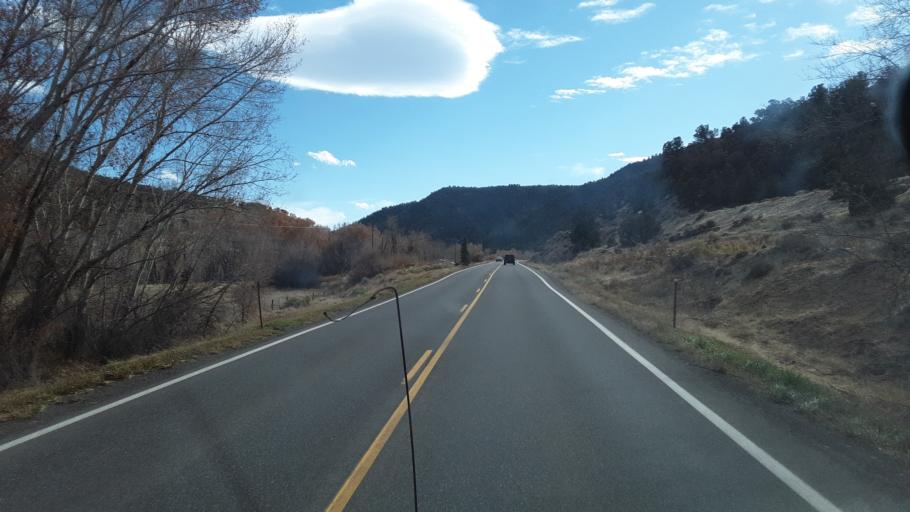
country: US
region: Colorado
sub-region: Montrose County
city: Montrose
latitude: 38.2805
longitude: -107.7650
